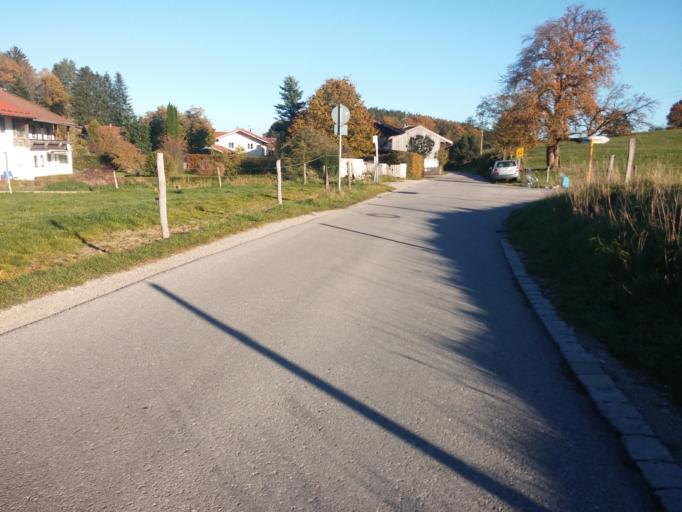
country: DE
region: Bavaria
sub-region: Upper Bavaria
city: Aying
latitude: 47.9616
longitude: 11.8013
